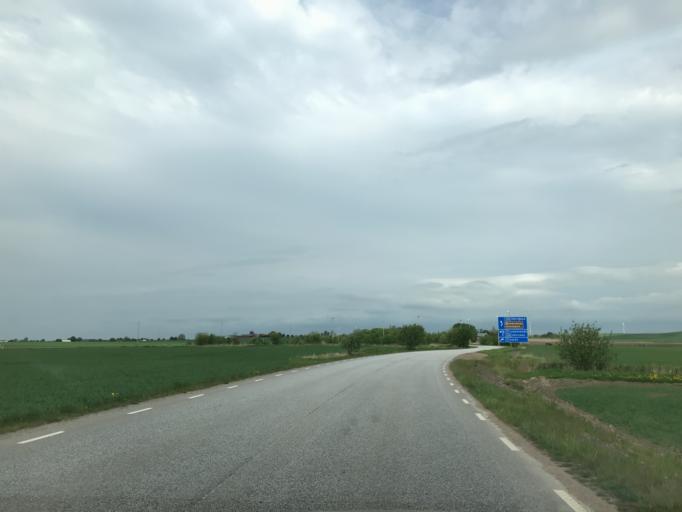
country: SE
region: Skane
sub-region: Svalovs Kommun
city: Svaloev
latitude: 55.8737
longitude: 13.1584
